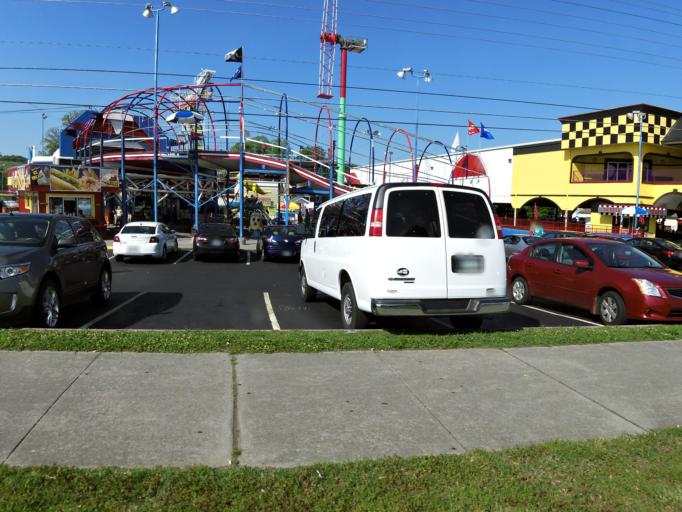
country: US
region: Tennessee
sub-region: Sevier County
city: Pigeon Forge
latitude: 35.7977
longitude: -83.5667
